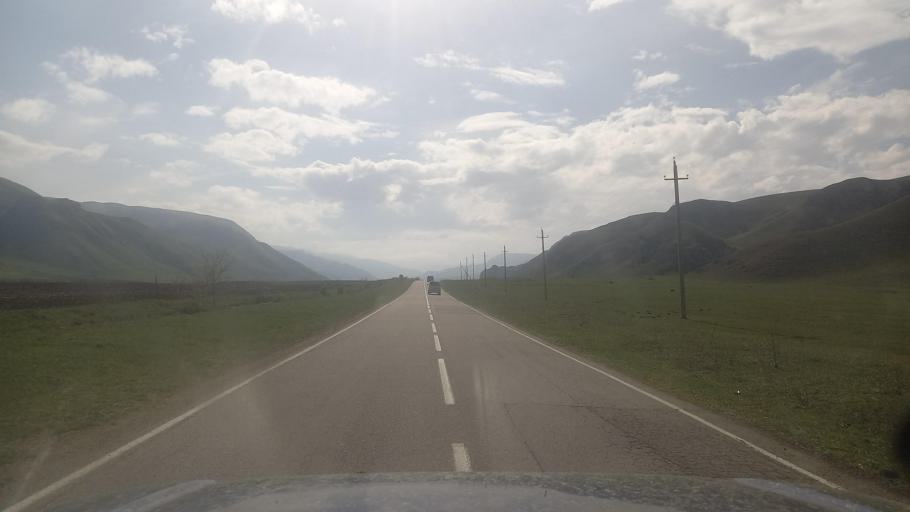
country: RU
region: Kabardino-Balkariya
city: Kamennomostskoye
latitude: 43.7352
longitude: 42.9832
